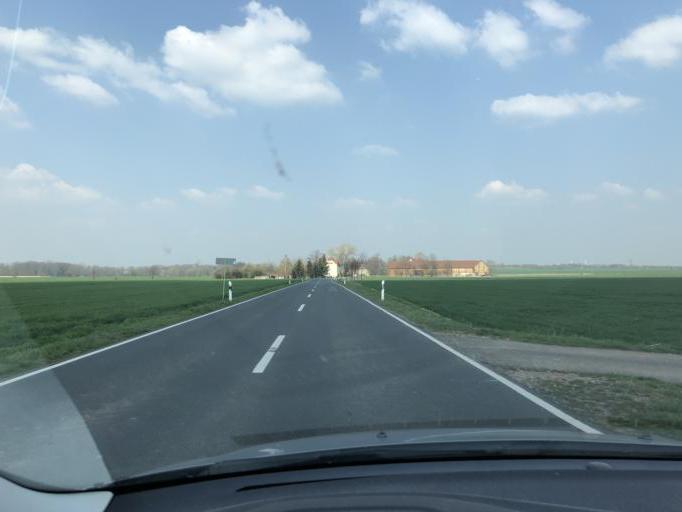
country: DE
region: Saxony-Anhalt
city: Landsberg
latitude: 51.5687
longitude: 12.1442
